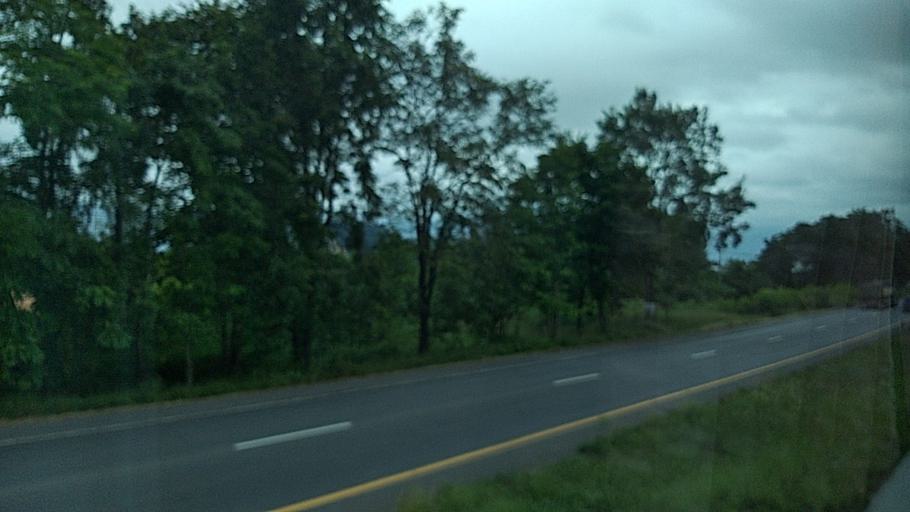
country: TH
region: Khon Kaen
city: Non Sila
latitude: 15.9102
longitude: 102.6577
